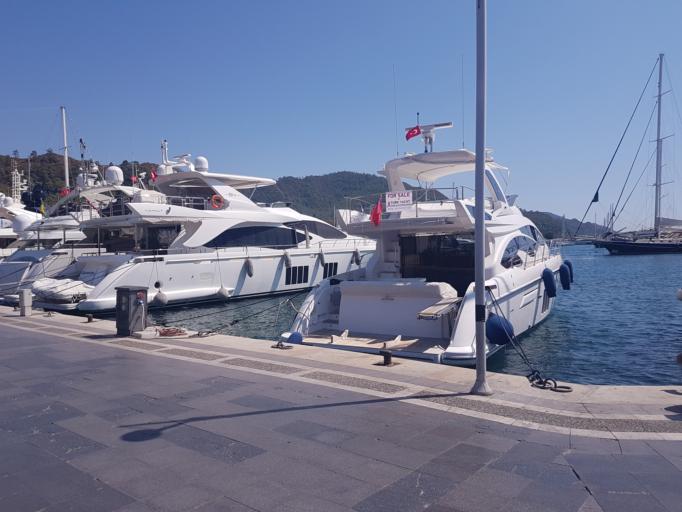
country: TR
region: Mugla
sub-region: Marmaris
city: Marmaris
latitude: 36.8526
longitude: 28.2759
